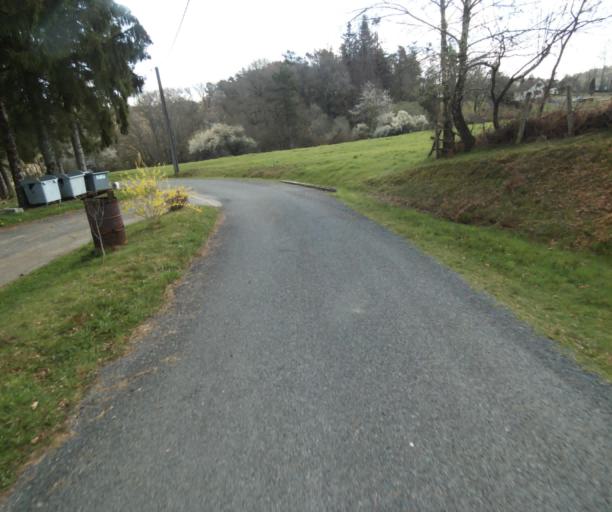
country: FR
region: Limousin
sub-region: Departement de la Correze
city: Laguenne
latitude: 45.2277
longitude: 1.8926
